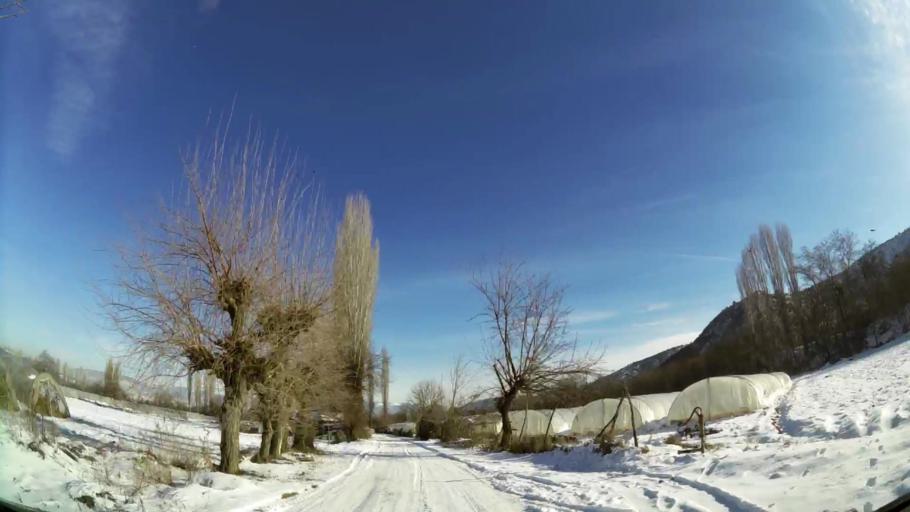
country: MK
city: Grchec
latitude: 41.9805
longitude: 21.3210
